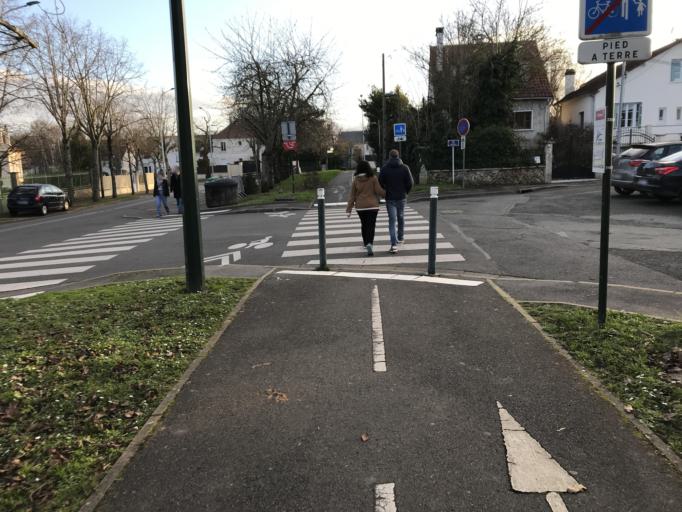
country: FR
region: Ile-de-France
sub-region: Departement de l'Essonne
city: Villebon-sur-Yvette
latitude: 48.7100
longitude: 2.2302
